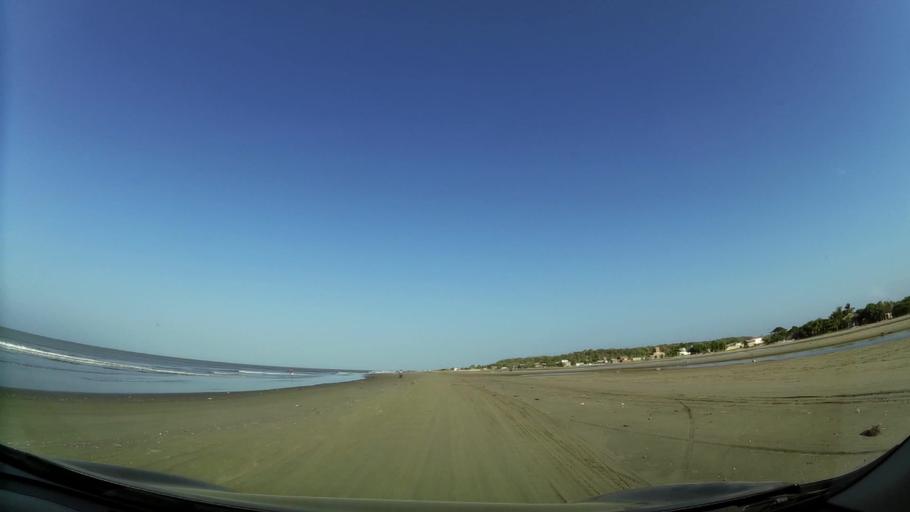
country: CO
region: Bolivar
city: Cartagena
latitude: 10.4920
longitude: -75.4945
